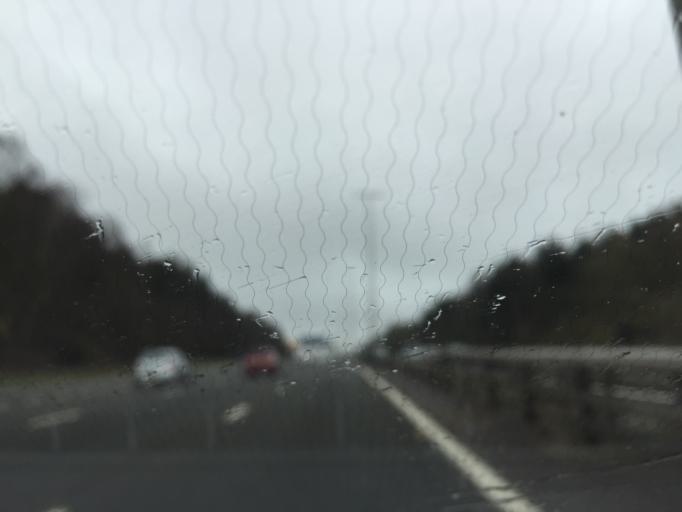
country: GB
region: England
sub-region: Hampshire
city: Hedge End
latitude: 50.9084
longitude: -1.3180
